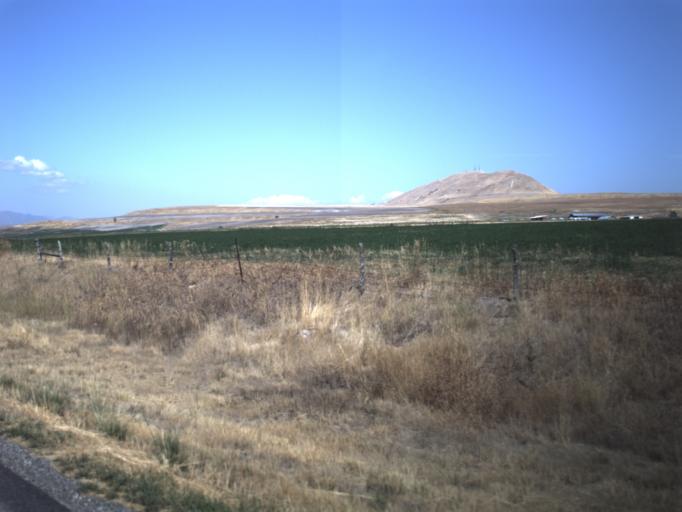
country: US
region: Utah
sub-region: Cache County
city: Benson
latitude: 41.8567
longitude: -111.9750
